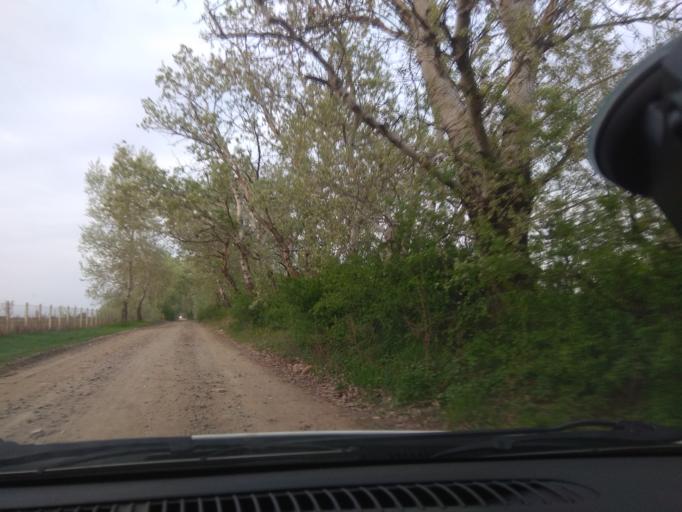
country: HU
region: Pest
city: Szigethalom
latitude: 47.3395
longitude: 19.0013
